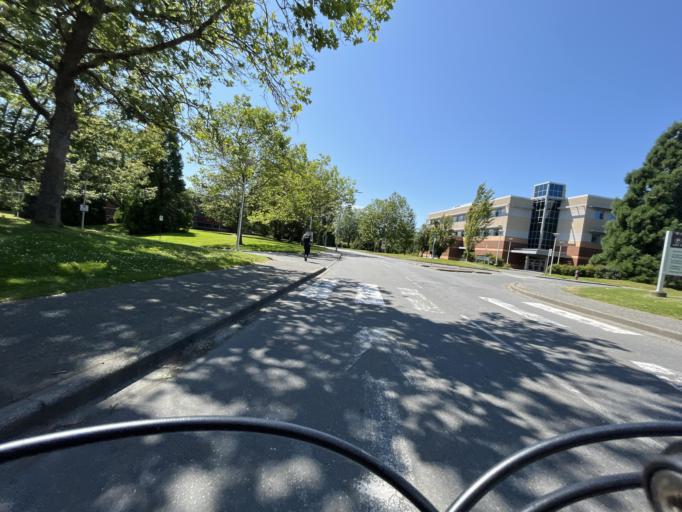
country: CA
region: British Columbia
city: Oak Bay
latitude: 48.4658
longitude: -123.3117
